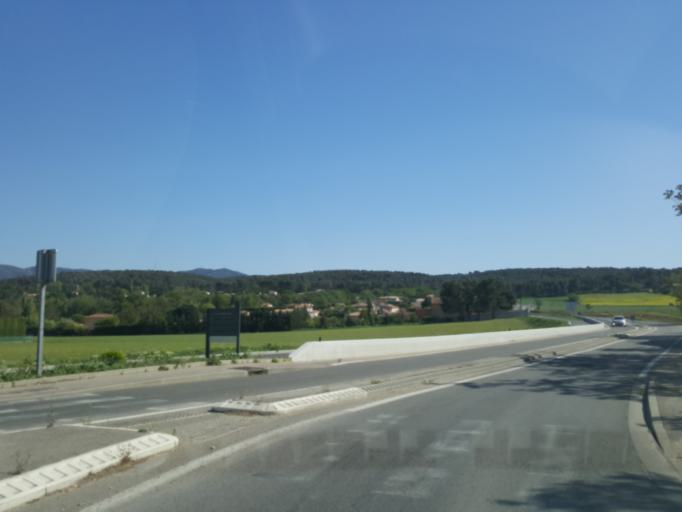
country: FR
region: Provence-Alpes-Cote d'Azur
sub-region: Departement des Bouches-du-Rhone
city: Cabries
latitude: 43.4458
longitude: 5.3607
